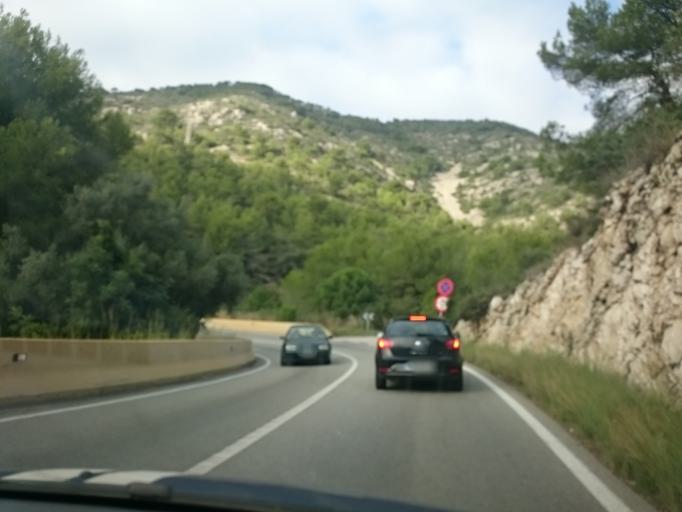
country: ES
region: Catalonia
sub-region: Provincia de Barcelona
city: Sitges
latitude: 41.2370
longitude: 1.8438
